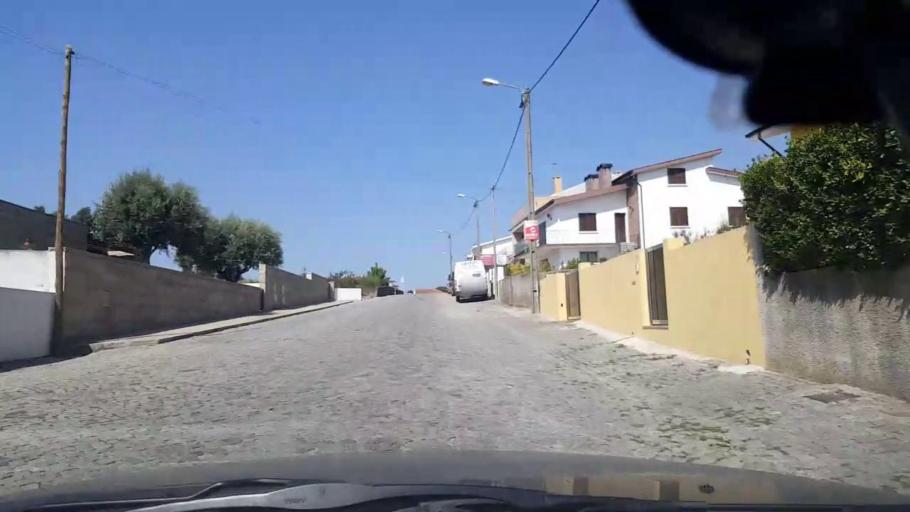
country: PT
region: Porto
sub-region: Vila do Conde
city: Arvore
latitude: 41.3773
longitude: -8.7031
